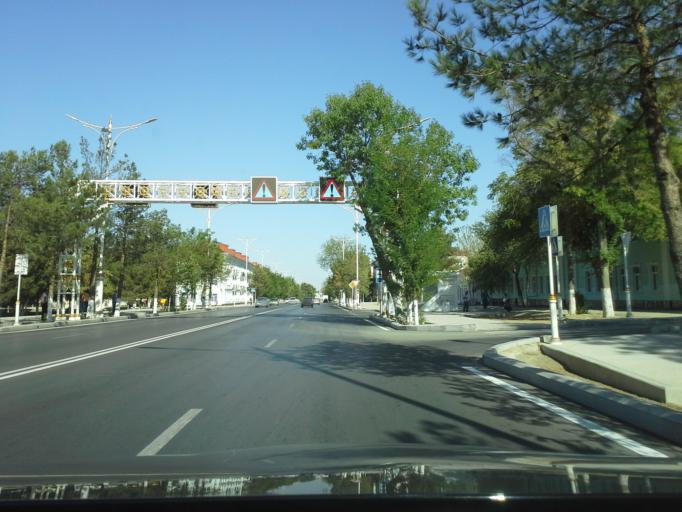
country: TM
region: Ahal
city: Ashgabat
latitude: 37.9581
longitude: 58.3473
